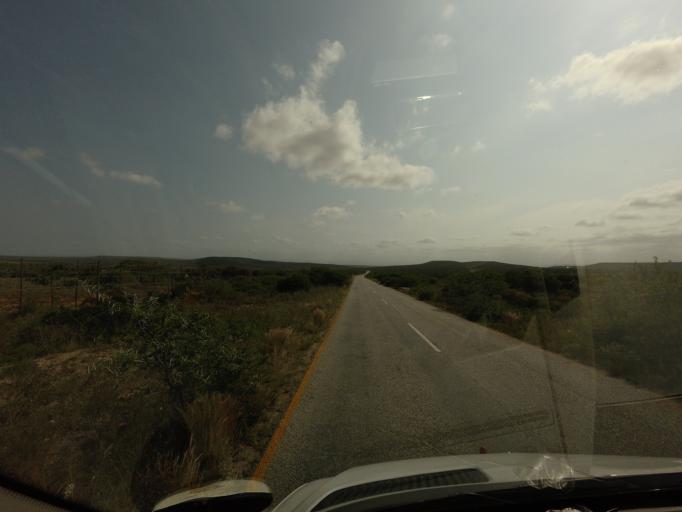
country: ZA
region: Eastern Cape
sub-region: Nelson Mandela Bay Metropolitan Municipality
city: Uitenhage
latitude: -33.6350
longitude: 25.5993
